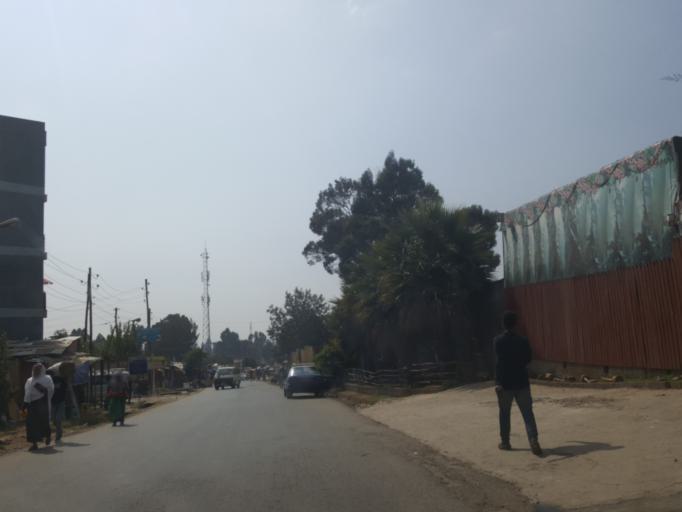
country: ET
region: Adis Abeba
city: Addis Ababa
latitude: 9.0557
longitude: 38.7196
